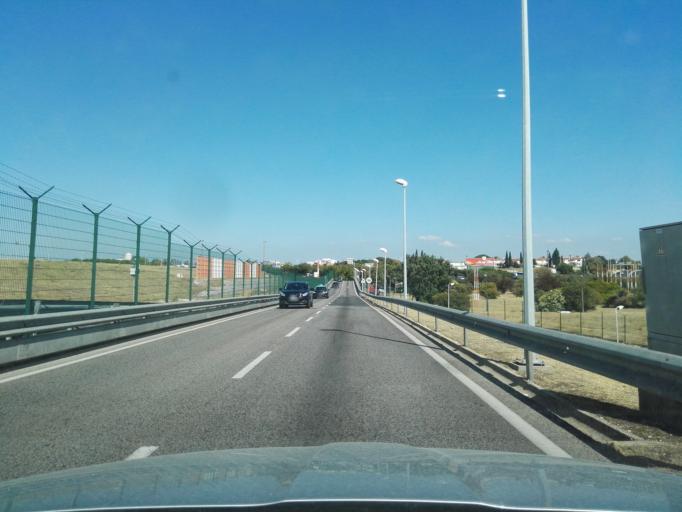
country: PT
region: Lisbon
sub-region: Loures
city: Moscavide
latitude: 38.7640
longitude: -9.1325
